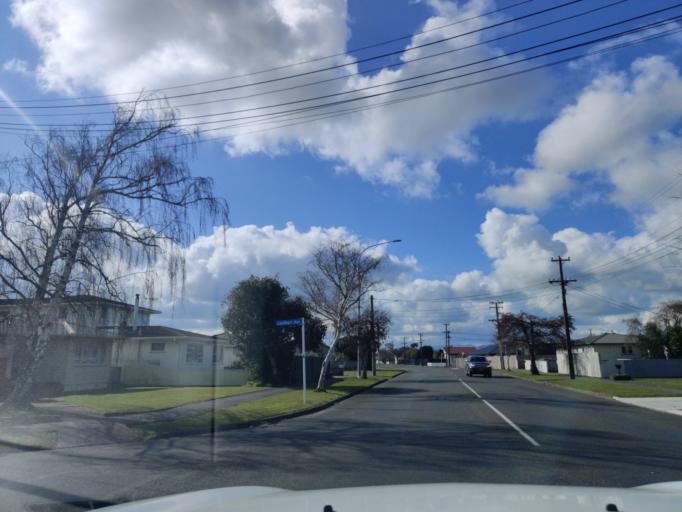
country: NZ
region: Manawatu-Wanganui
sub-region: Palmerston North City
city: Palmerston North
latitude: -40.3342
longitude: 175.6109
